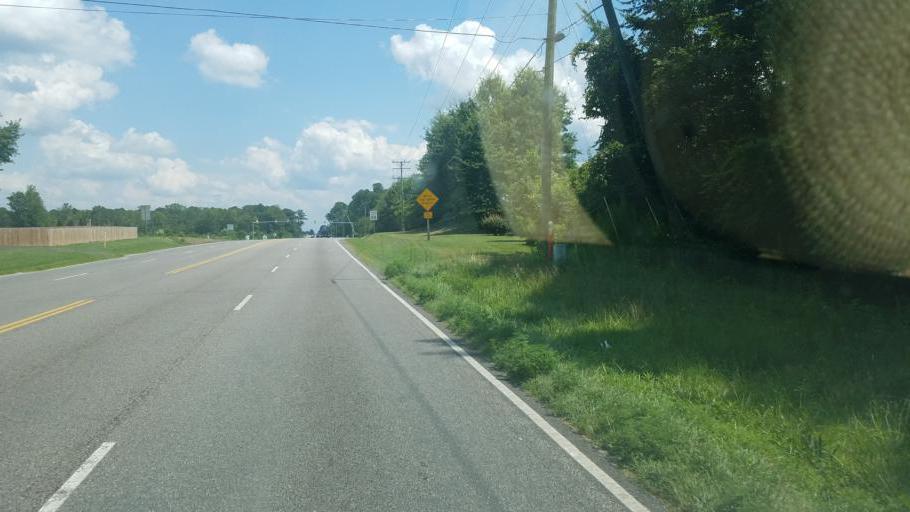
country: US
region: Virginia
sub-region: Isle of Wight County
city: Windsor
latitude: 36.8020
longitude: -76.7179
